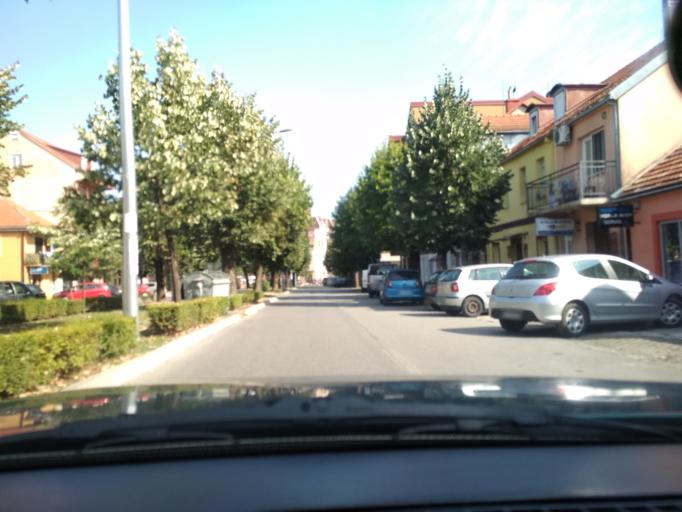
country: ME
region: Cetinje
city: Cetinje
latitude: 42.3924
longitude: 18.9205
